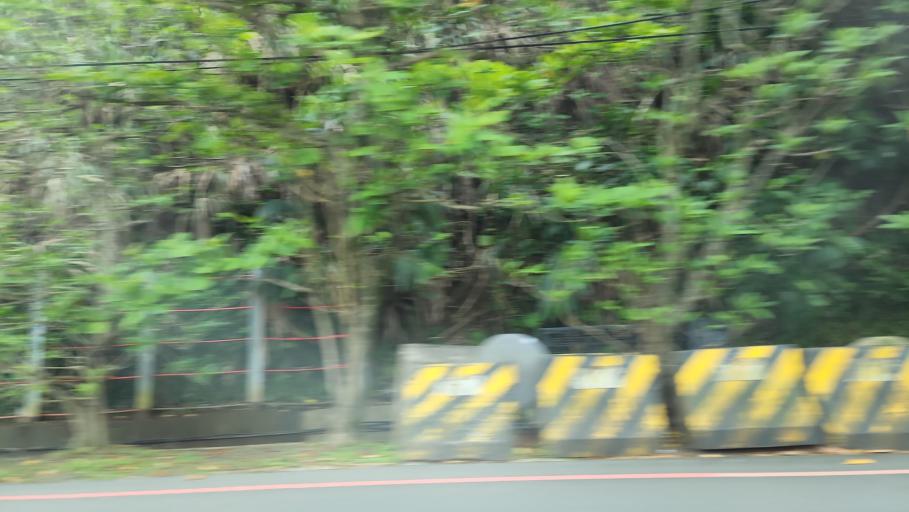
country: TW
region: Taiwan
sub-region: Keelung
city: Keelung
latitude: 25.1639
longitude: 121.7220
